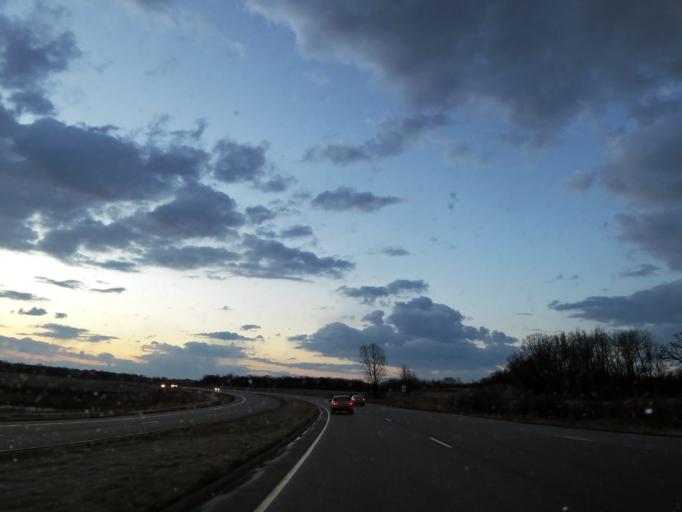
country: US
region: Minnesota
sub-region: Scott County
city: Prior Lake
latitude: 44.6857
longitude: -93.3661
